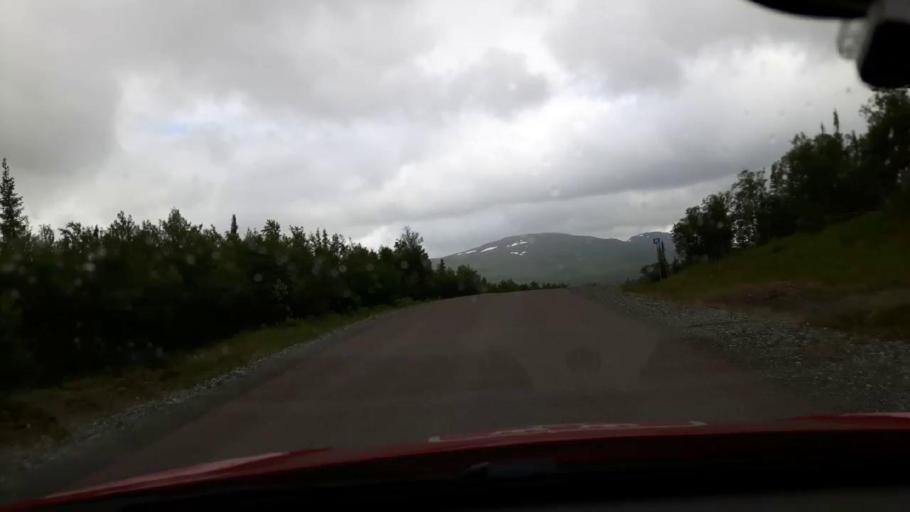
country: SE
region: Jaemtland
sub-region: Are Kommun
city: Are
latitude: 63.2384
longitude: 12.4306
